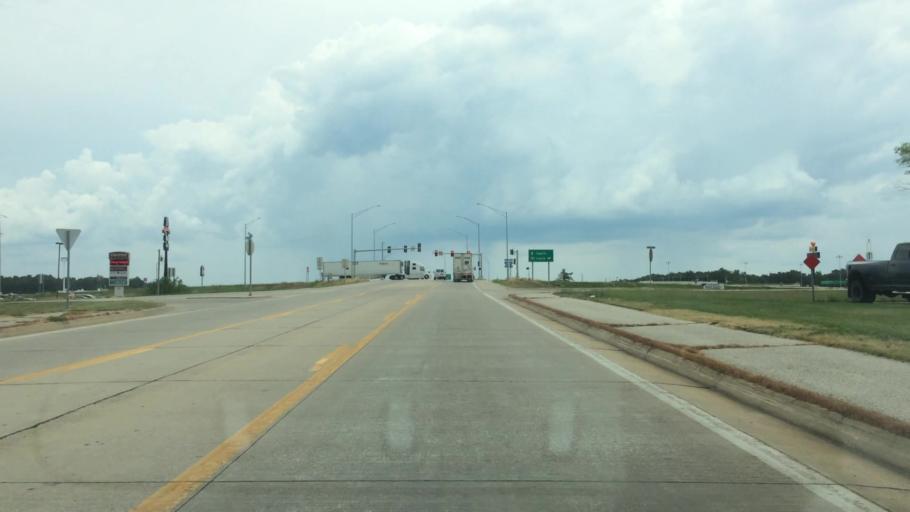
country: US
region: Missouri
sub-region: Greene County
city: Strafford
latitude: 37.2700
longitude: -93.1135
